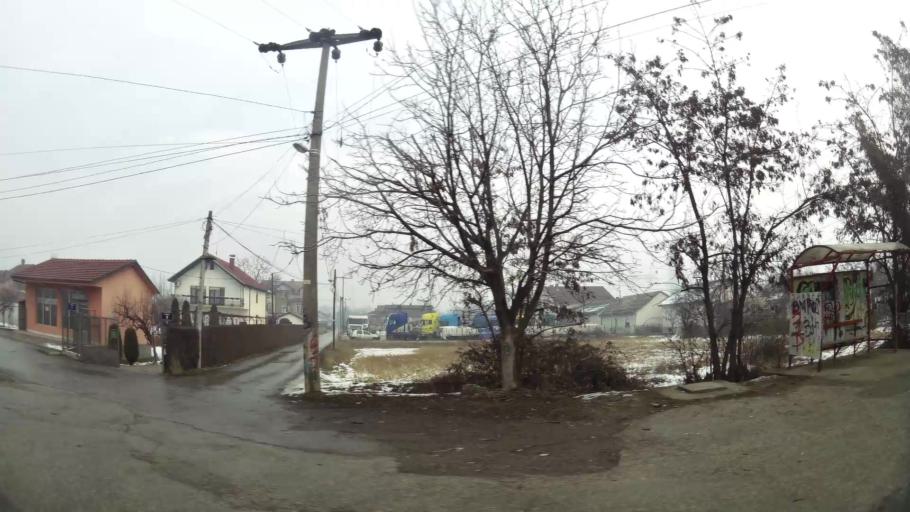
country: MK
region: Ilinden
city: Jurumleri
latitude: 41.9688
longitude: 21.5473
